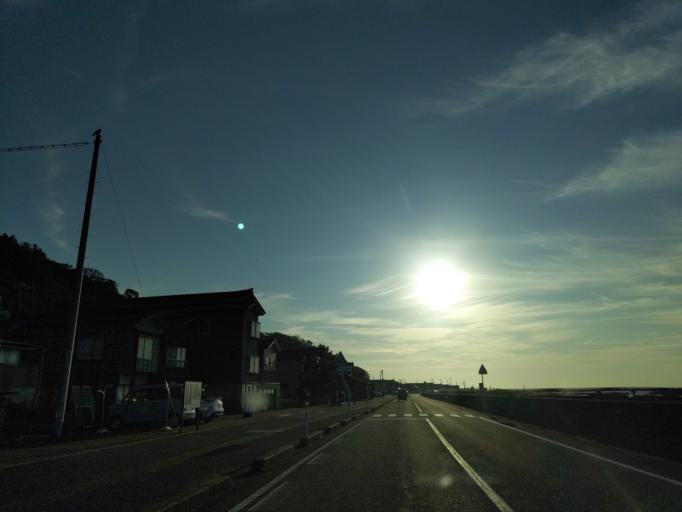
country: JP
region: Niigata
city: Nagaoka
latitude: 37.5466
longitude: 138.6945
